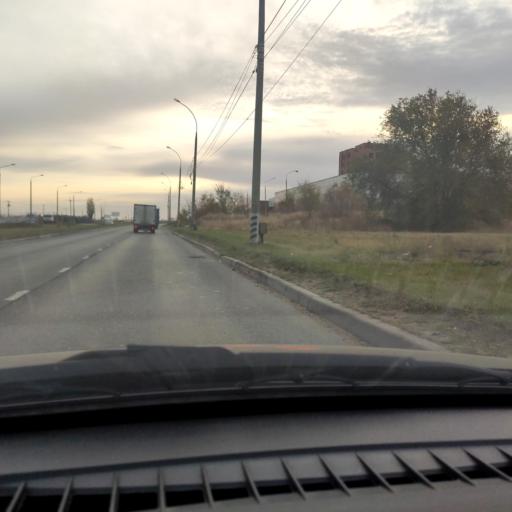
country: RU
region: Samara
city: Tol'yatti
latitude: 53.5565
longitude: 49.3414
